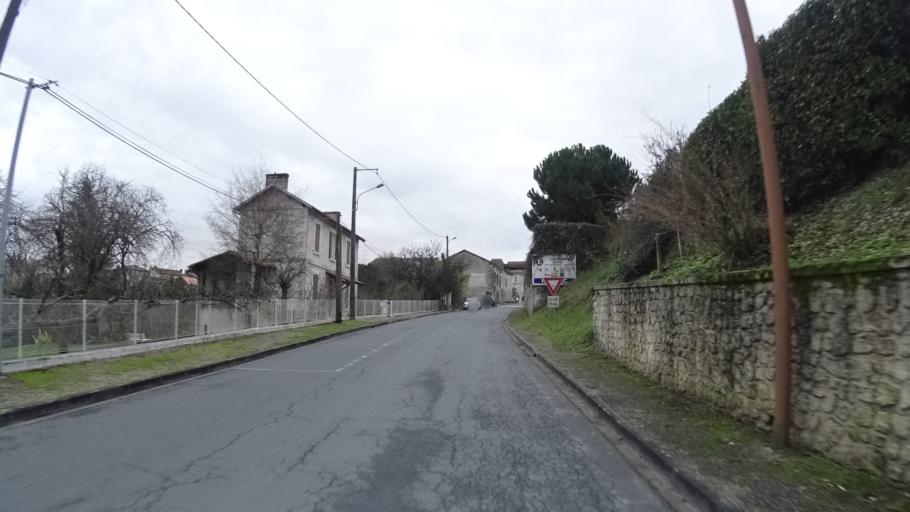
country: FR
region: Aquitaine
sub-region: Departement de la Dordogne
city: Saint-Aulaye
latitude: 45.2043
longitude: 0.1346
